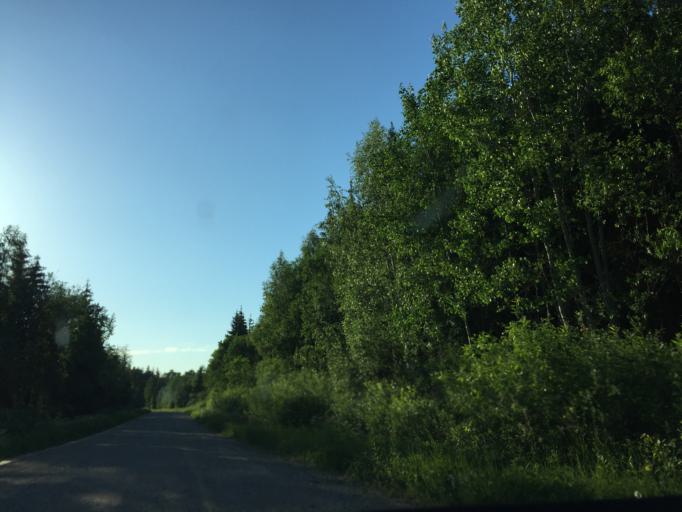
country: LV
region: Talsu Rajons
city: Sabile
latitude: 56.8684
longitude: 22.6374
